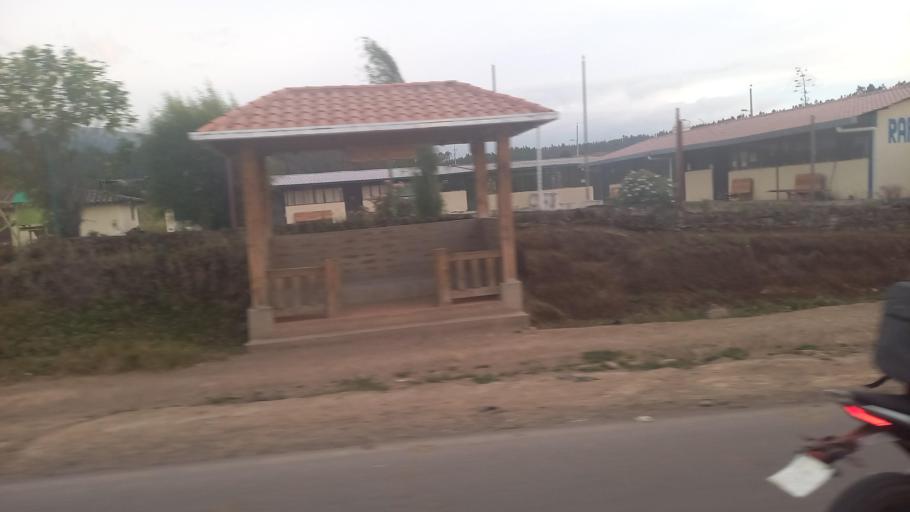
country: EC
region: Pichincha
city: Cayambe
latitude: 0.0709
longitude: -78.1108
